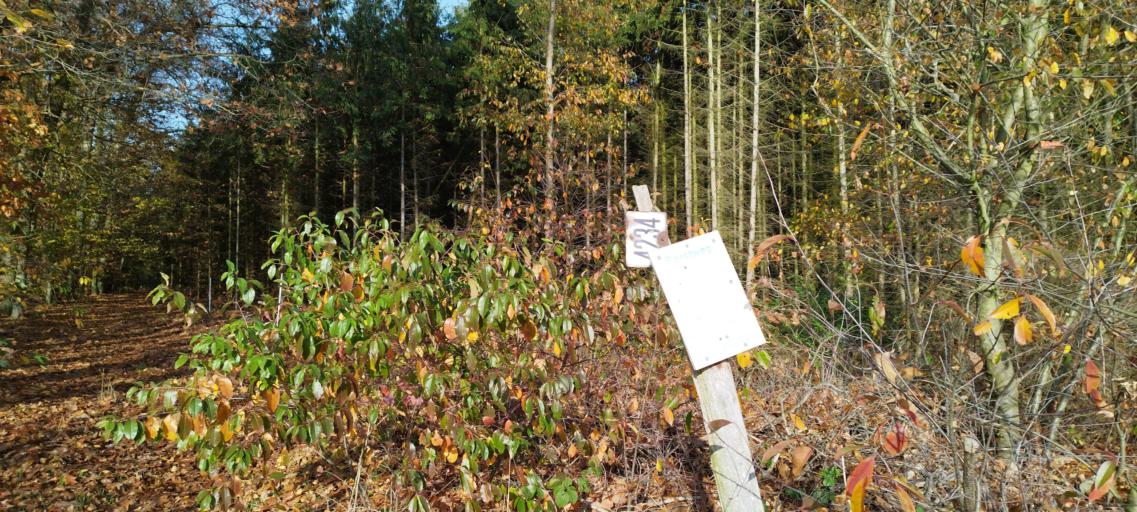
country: DE
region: Brandenburg
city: Strausberg
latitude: 52.6260
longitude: 13.8837
